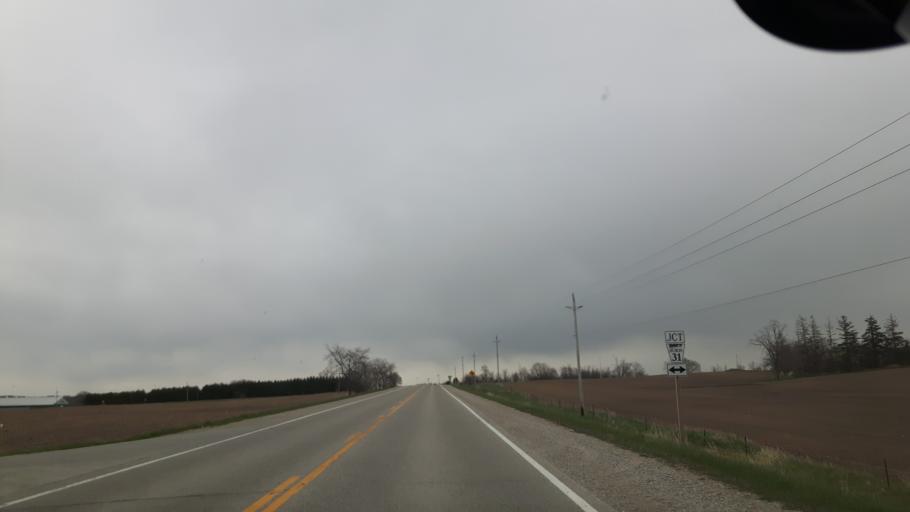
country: CA
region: Ontario
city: Bluewater
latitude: 43.5869
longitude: -81.6064
